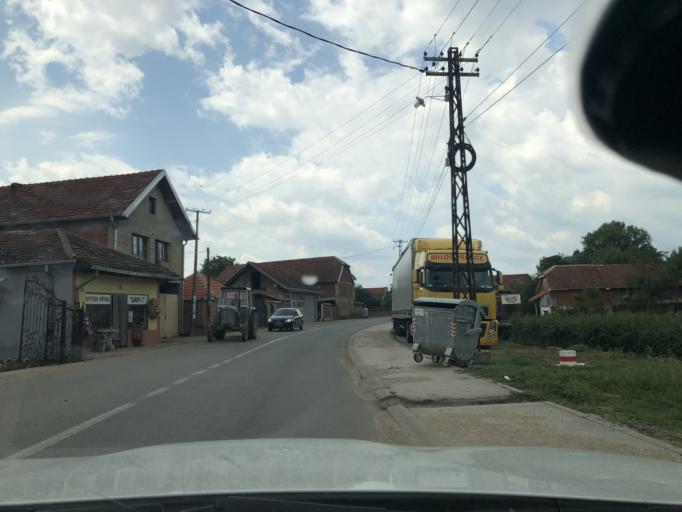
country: RS
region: Central Serbia
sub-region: Jablanicki Okrug
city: Lebane
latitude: 42.9473
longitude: 21.8268
